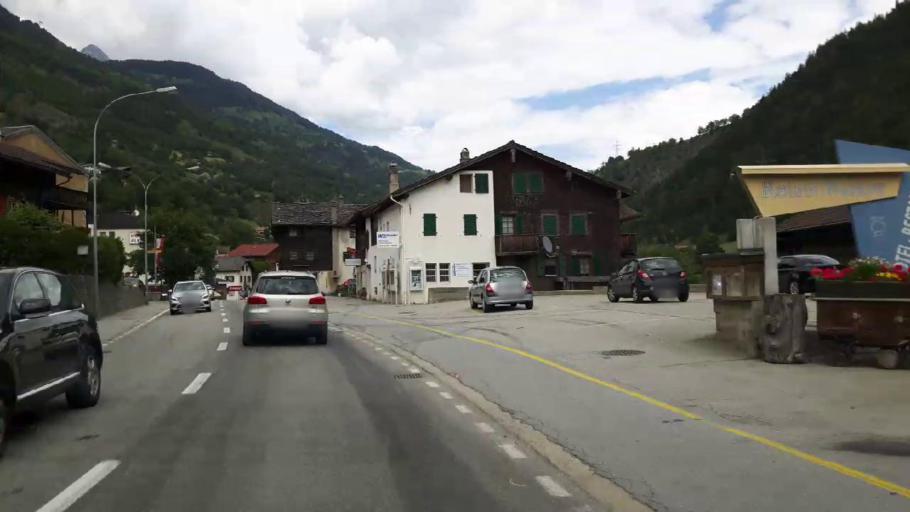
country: CH
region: Valais
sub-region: Brig District
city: Naters
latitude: 46.3554
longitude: 8.0453
